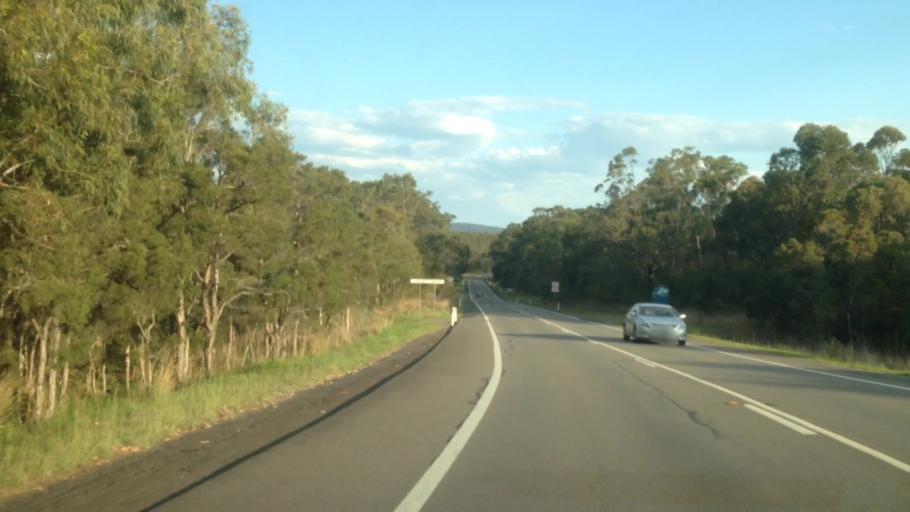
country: AU
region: New South Wales
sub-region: Cessnock
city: Kurri Kurri
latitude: -32.8346
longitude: 151.4806
